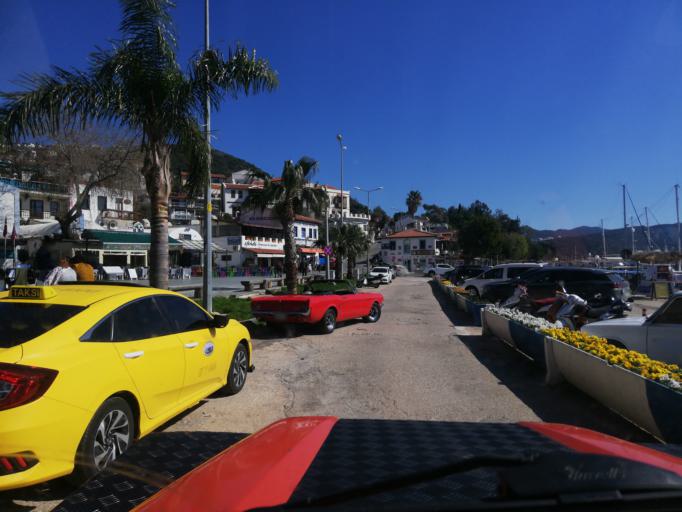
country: TR
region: Antalya
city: Kas
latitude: 36.1992
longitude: 29.6411
